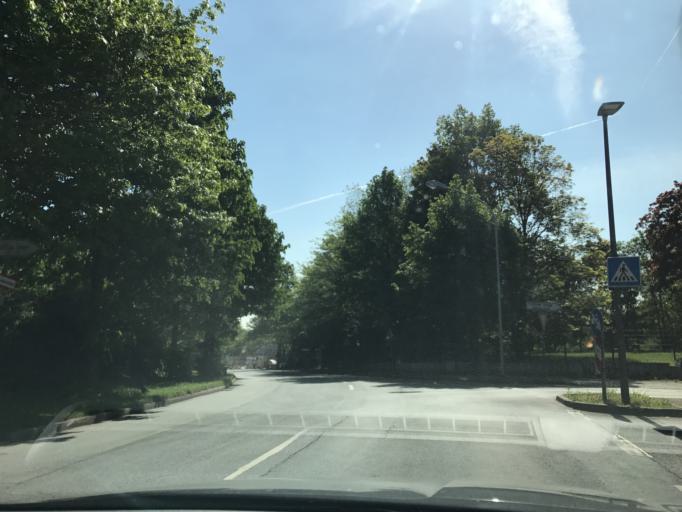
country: DE
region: North Rhine-Westphalia
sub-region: Regierungsbezirk Dusseldorf
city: Essen
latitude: 51.4285
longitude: 7.0099
